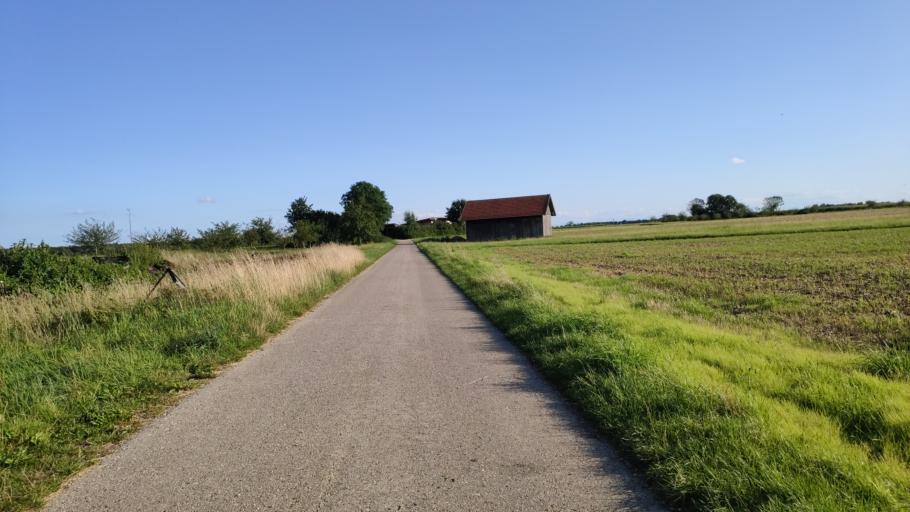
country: DE
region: Bavaria
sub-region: Swabia
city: Oberottmarshausen
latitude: 48.2300
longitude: 10.8591
